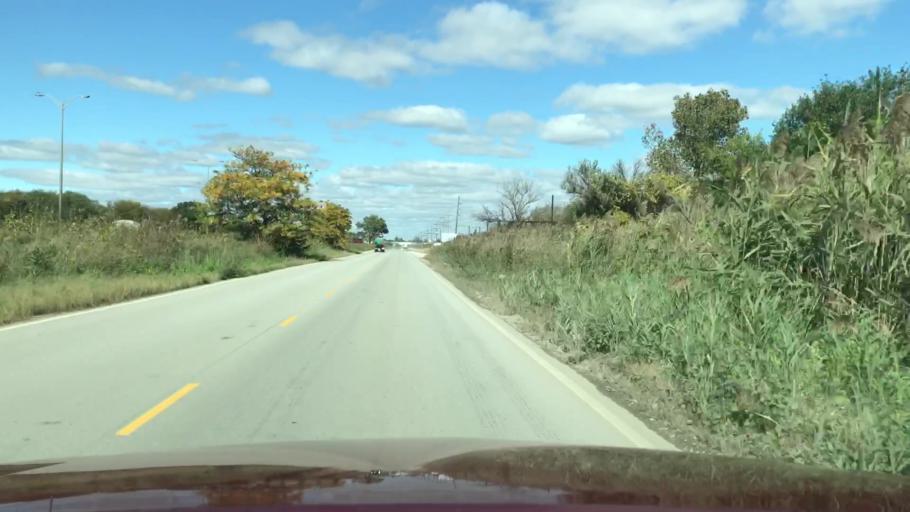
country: US
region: Illinois
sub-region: Cook County
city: Dolton
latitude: 41.6657
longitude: -87.5933
